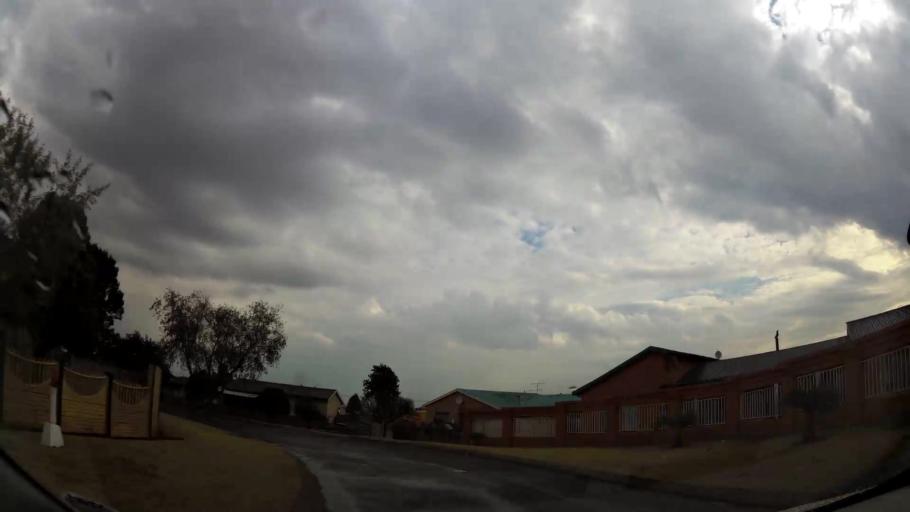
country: ZA
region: Gauteng
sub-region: Ekurhuleni Metropolitan Municipality
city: Germiston
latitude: -26.3826
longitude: 28.1312
